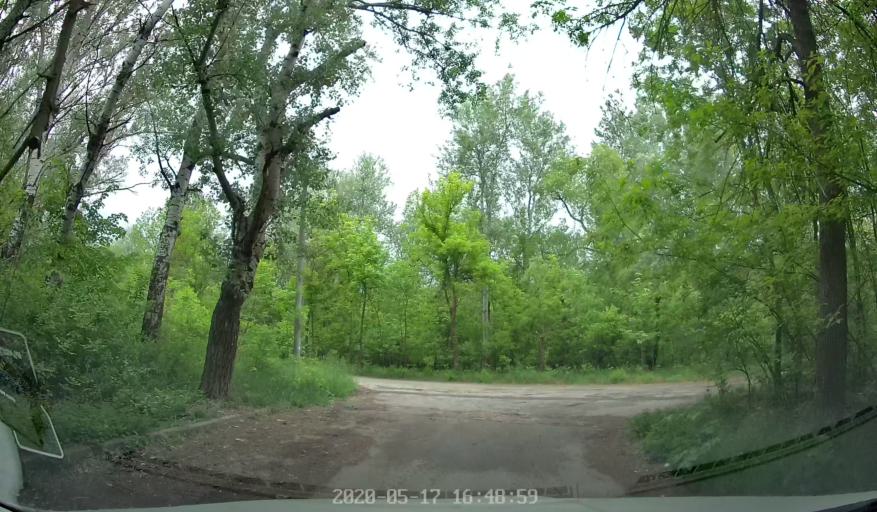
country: MD
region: Chisinau
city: Vatra
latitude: 47.0519
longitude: 28.7881
